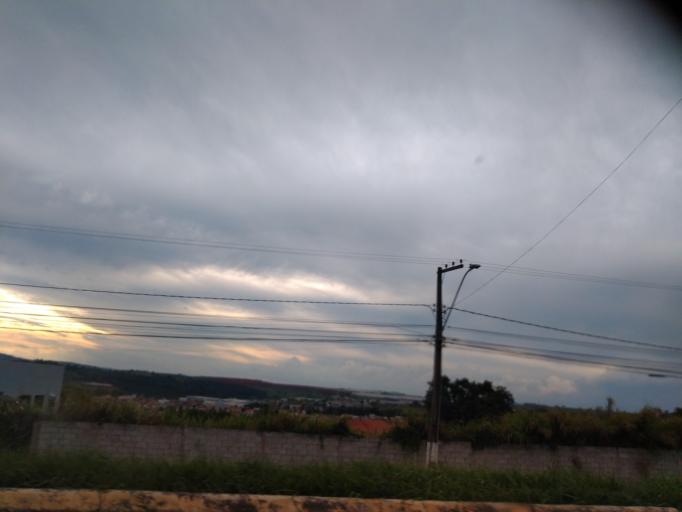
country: BR
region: Minas Gerais
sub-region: Varginha
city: Varginha
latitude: -21.5954
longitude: -45.4396
